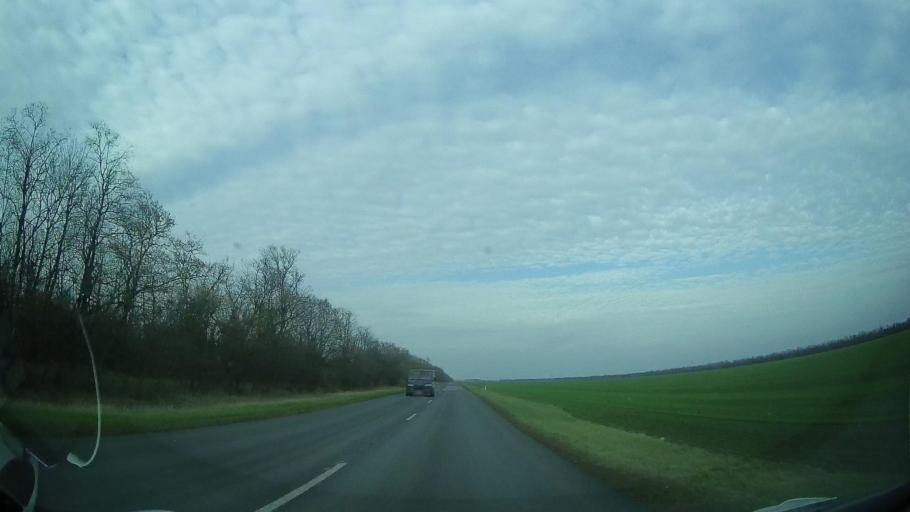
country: RU
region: Rostov
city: Zernograd
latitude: 46.9449
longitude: 40.3666
